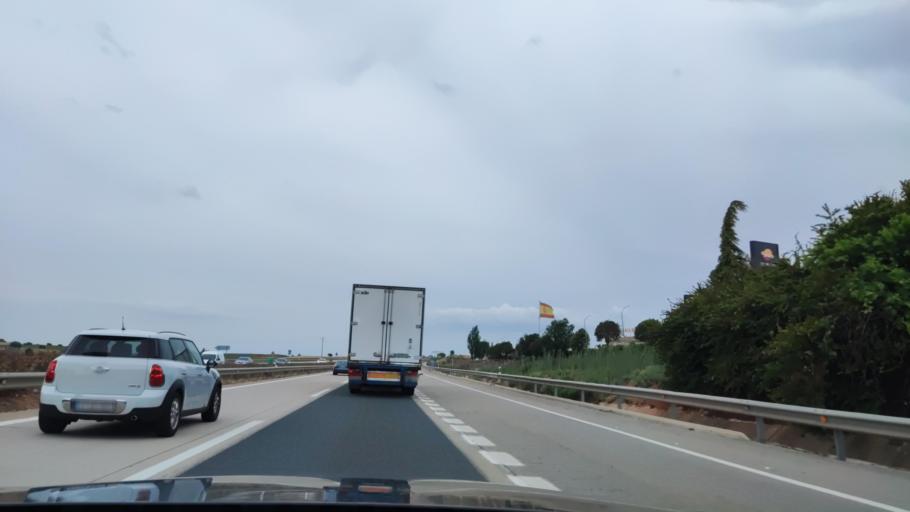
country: ES
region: Castille-La Mancha
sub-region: Provincia de Cuenca
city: Honrubia
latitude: 39.5990
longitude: -2.2813
